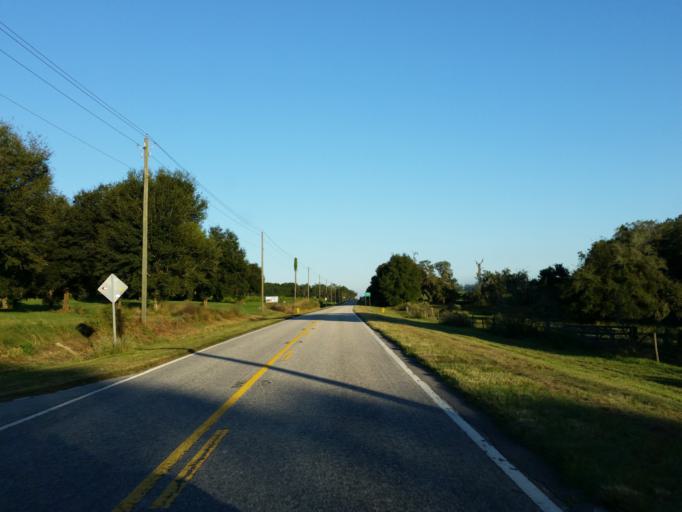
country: US
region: Florida
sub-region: Pasco County
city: Dade City North
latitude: 28.4162
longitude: -82.2647
